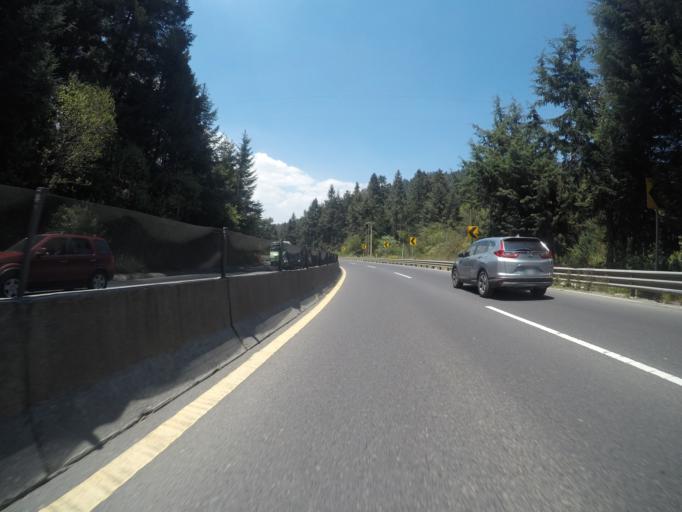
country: MX
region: Mexico City
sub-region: Cuajimalpa de Morelos
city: San Lorenzo Acopilco
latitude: 19.2950
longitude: -99.3555
